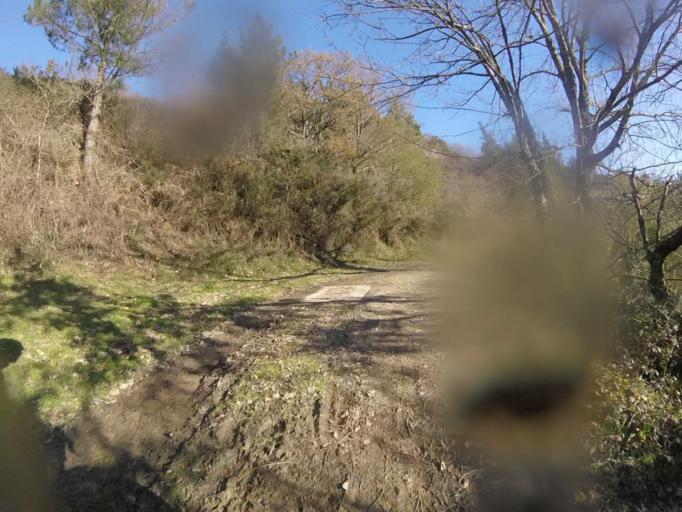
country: ES
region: Navarre
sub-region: Provincia de Navarra
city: Bera
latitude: 43.3028
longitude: -1.6806
